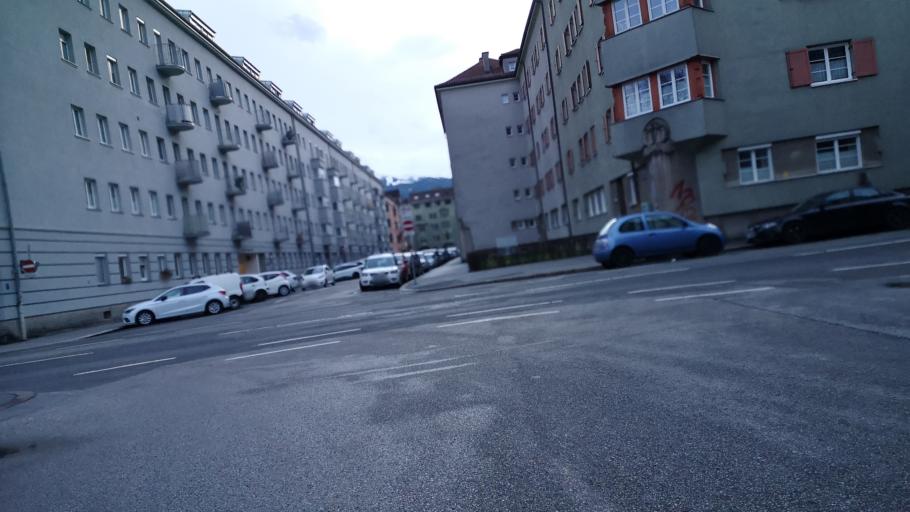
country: AT
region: Tyrol
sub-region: Innsbruck Stadt
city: Innsbruck
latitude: 47.2758
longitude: 11.4092
